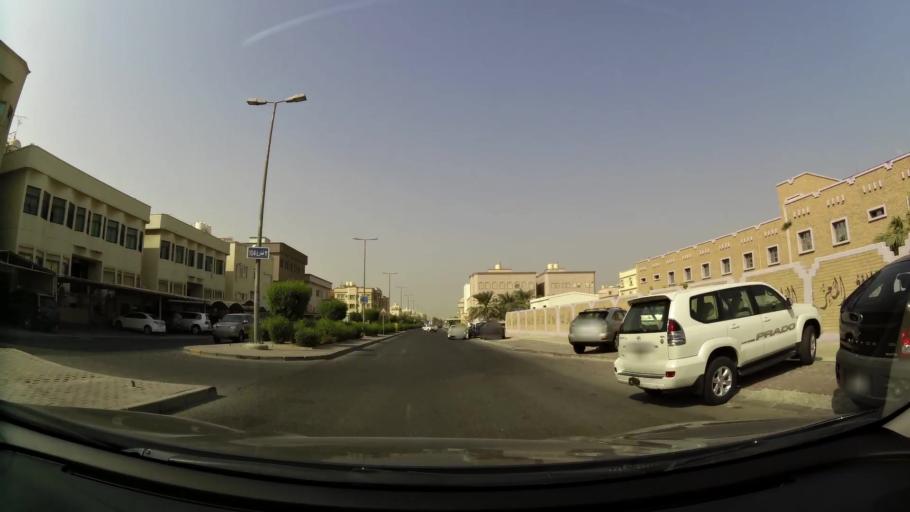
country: KW
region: Al Asimah
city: Ar Rabiyah
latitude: 29.2708
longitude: 47.8862
